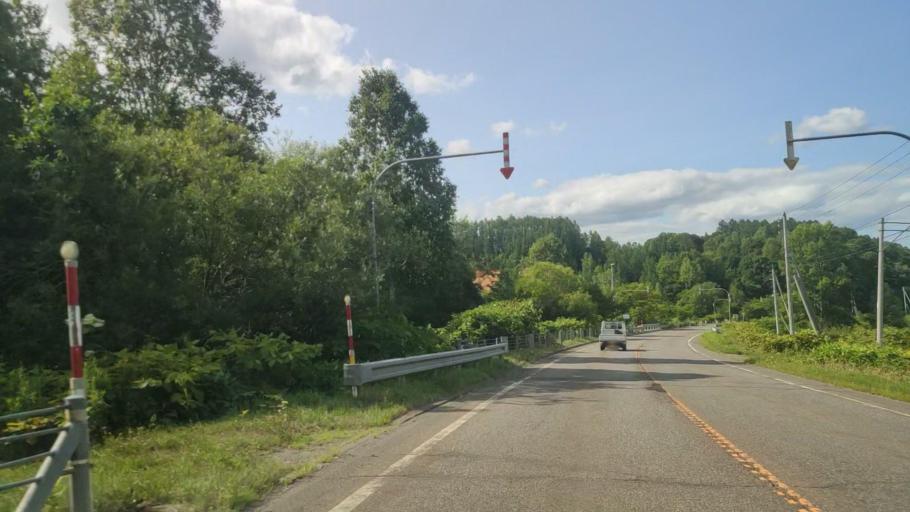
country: JP
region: Hokkaido
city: Nayoro
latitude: 44.3933
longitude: 142.3944
